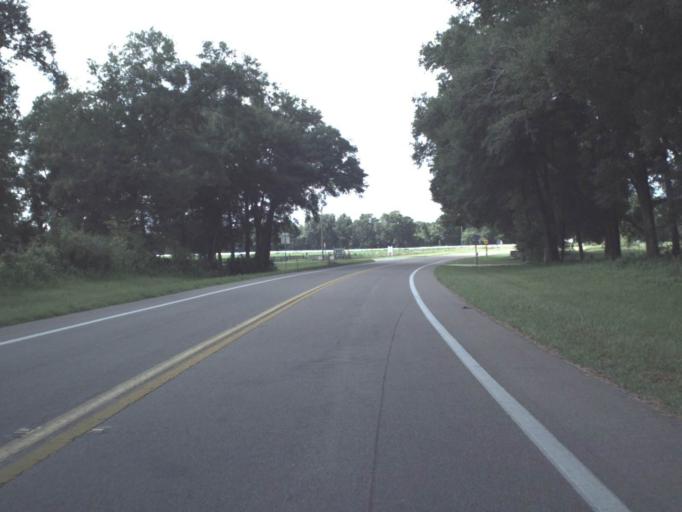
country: US
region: Florida
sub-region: Gilchrist County
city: Trenton
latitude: 29.6749
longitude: -82.8563
